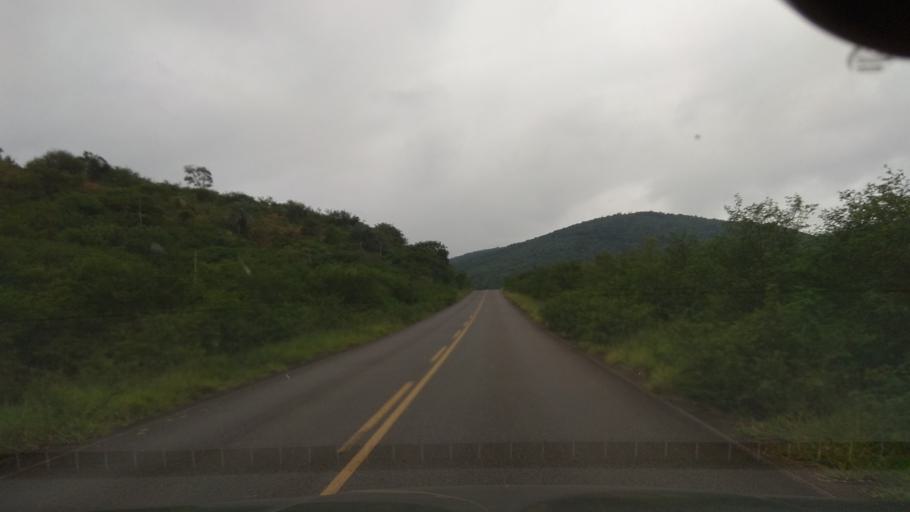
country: BR
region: Bahia
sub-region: Santa Ines
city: Santa Ines
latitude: -13.2517
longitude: -39.7750
